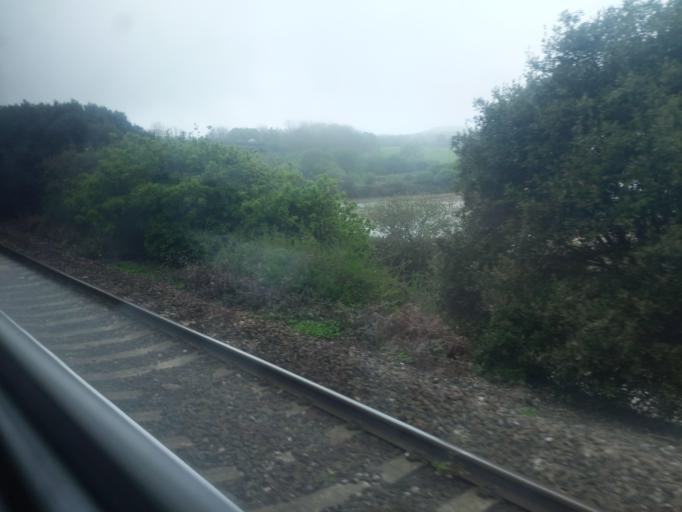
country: GB
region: England
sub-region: Cornwall
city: Hayle
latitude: 50.1753
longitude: -5.4322
